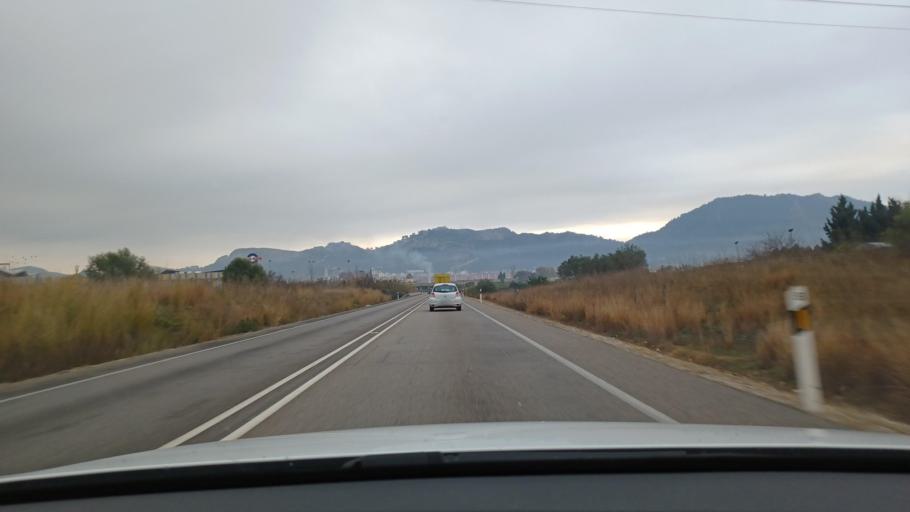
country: ES
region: Valencia
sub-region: Provincia de Valencia
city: Llosa de Ranes
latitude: 39.0057
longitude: -0.5310
